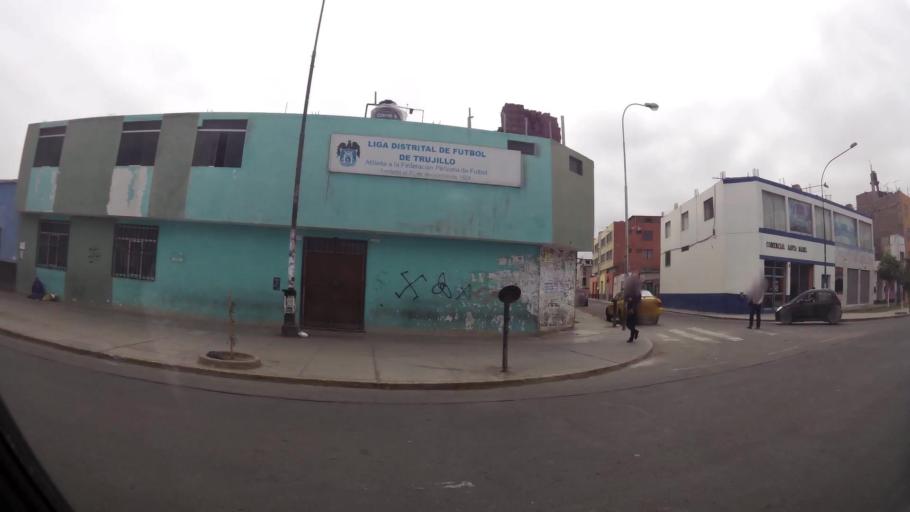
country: PE
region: La Libertad
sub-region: Provincia de Trujillo
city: Trujillo
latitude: -8.1098
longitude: -79.0218
